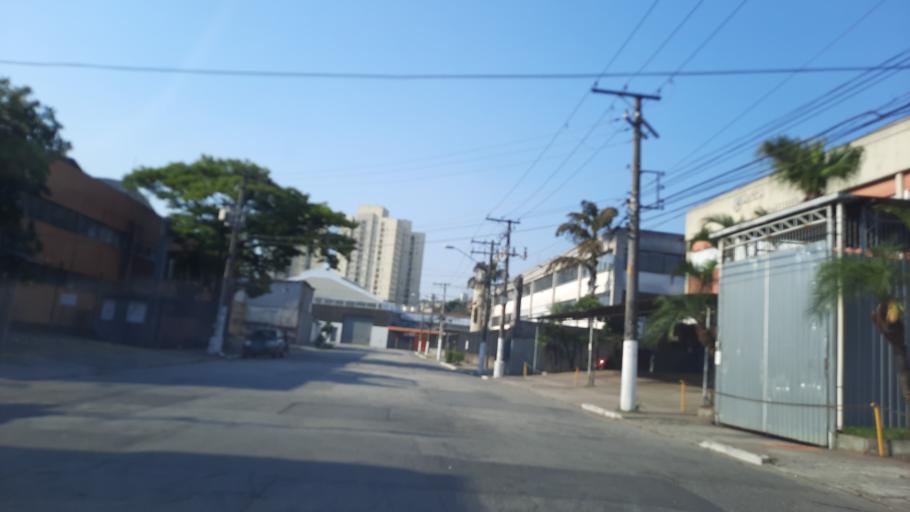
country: BR
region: Sao Paulo
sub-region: Sao Paulo
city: Sao Paulo
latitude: -23.5060
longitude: -46.6827
